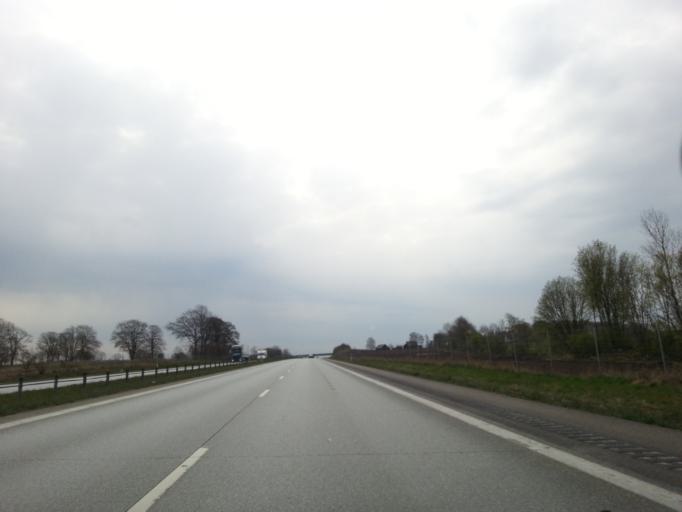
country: SE
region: Halland
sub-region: Falkenbergs Kommun
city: Falkenberg
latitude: 56.9277
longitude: 12.5263
